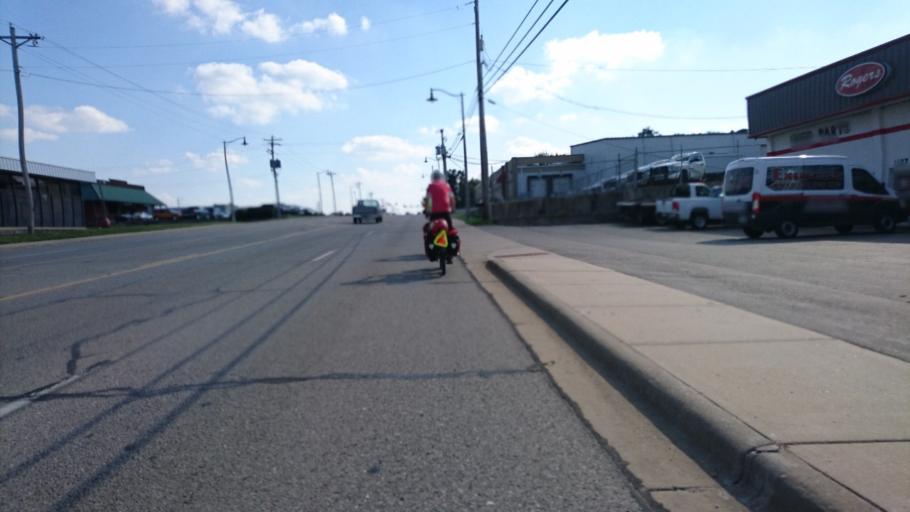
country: US
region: Missouri
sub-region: Laclede County
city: Lebanon
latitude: 37.6649
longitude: -92.6677
